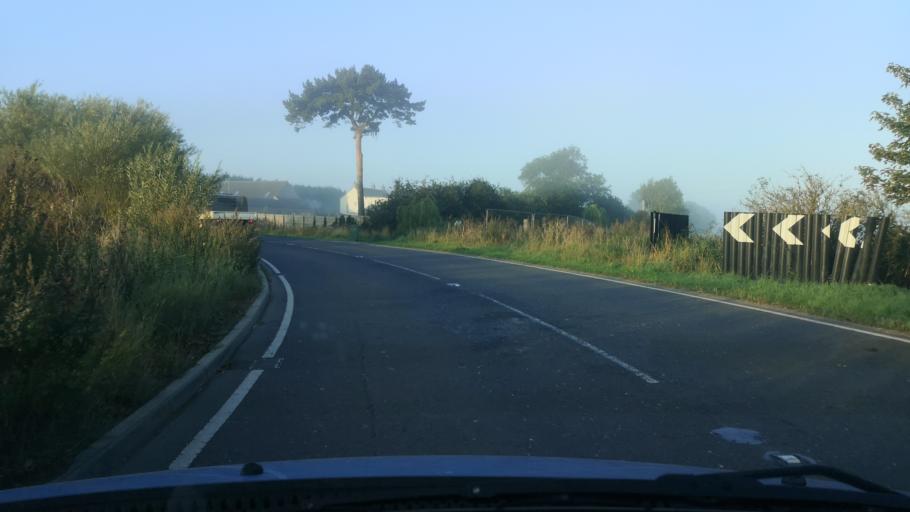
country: GB
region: England
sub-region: North Lincolnshire
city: Eastoft
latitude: 53.6574
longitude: -0.7766
